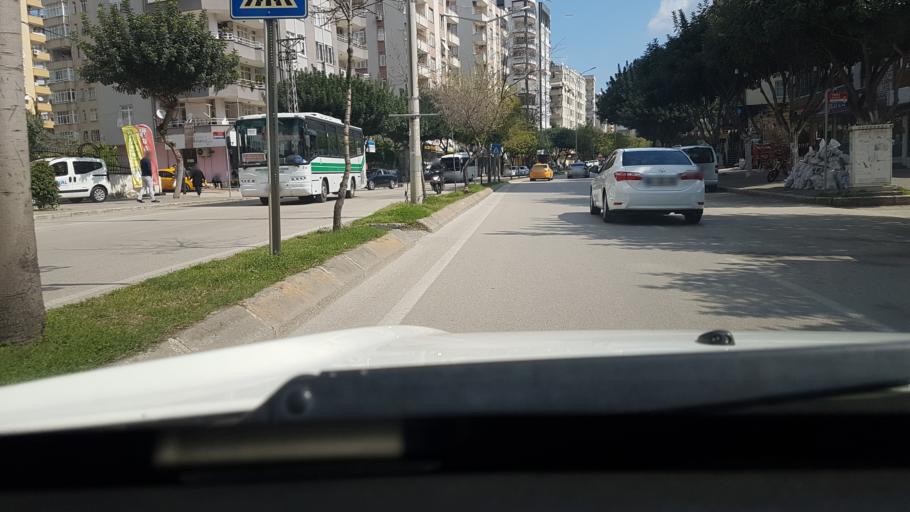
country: TR
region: Adana
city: Adana
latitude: 37.0378
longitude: 35.2998
